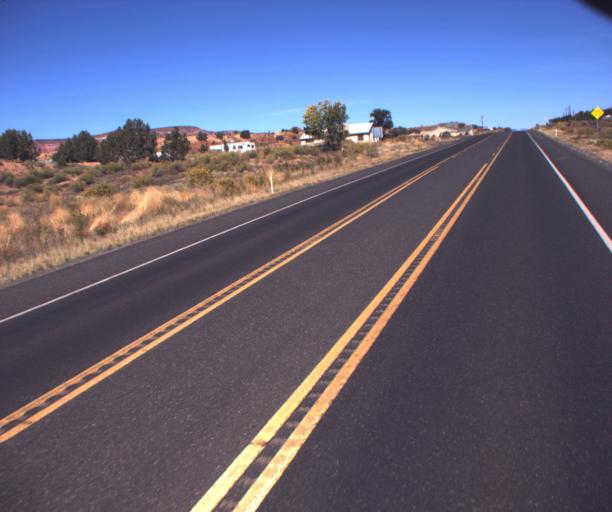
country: US
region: Arizona
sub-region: Coconino County
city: Fredonia
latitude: 36.9873
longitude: -112.5301
